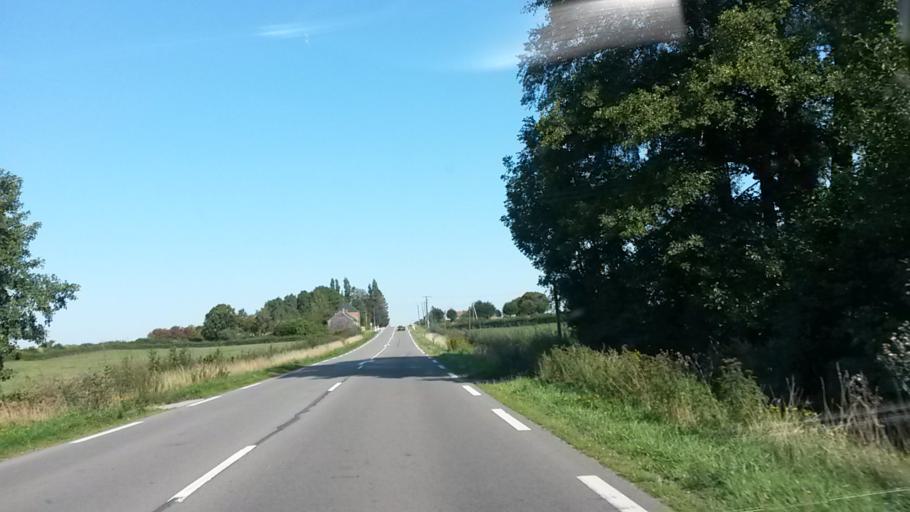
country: FR
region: Nord-Pas-de-Calais
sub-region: Departement du Nord
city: Avesnelles
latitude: 50.1670
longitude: 3.9537
